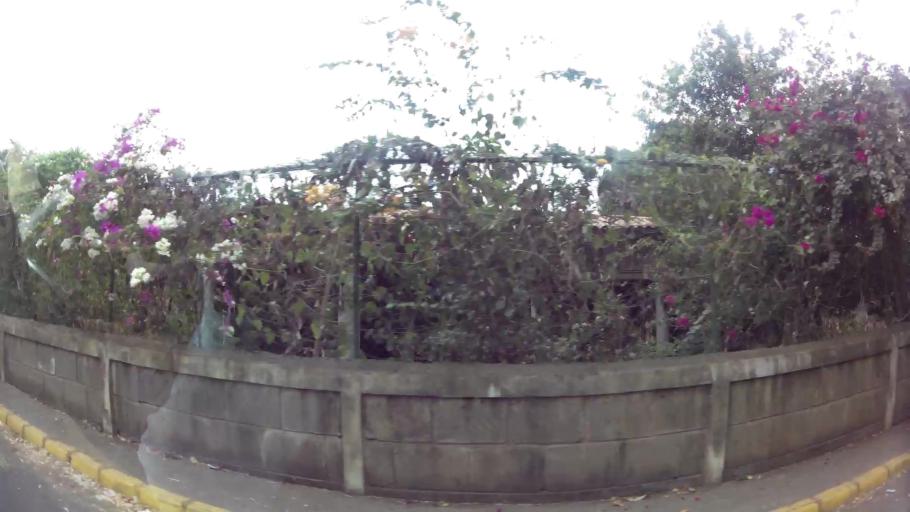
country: NI
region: Masaya
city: Ticuantepe
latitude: 12.0573
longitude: -86.1953
